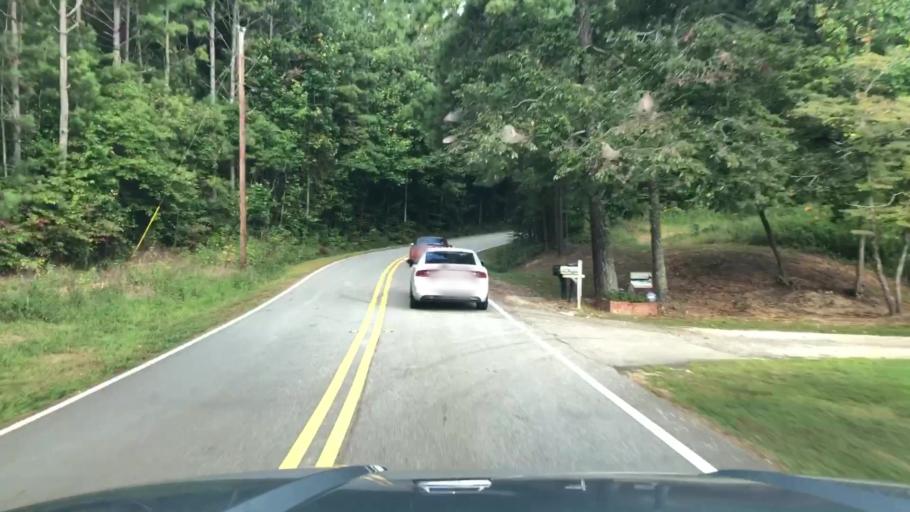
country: US
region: Georgia
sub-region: Paulding County
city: Dallas
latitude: 34.0392
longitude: -84.8632
